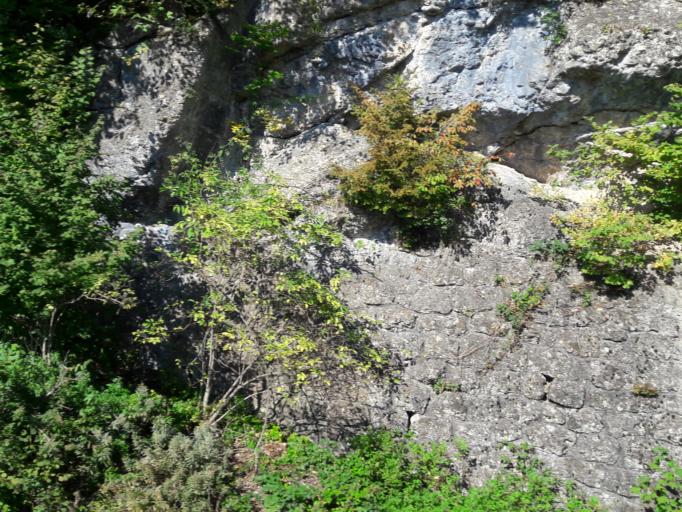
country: CH
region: Schwyz
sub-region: Bezirk Schwyz
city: Steinen
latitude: 47.0567
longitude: 8.5984
